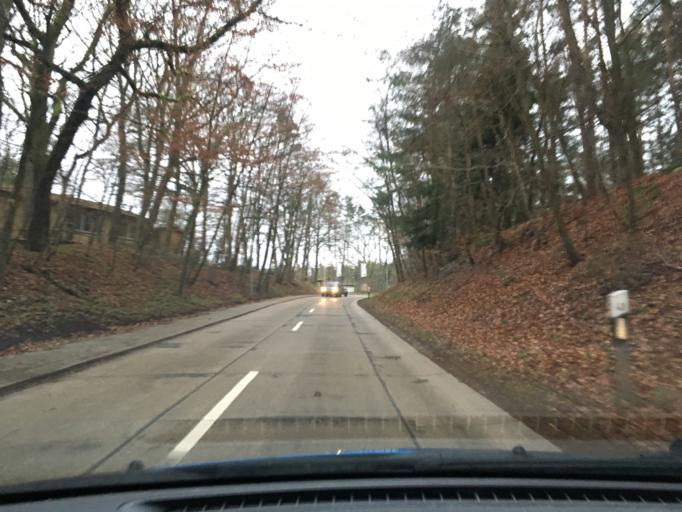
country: DE
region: Lower Saxony
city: Tosterglope
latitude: 53.2604
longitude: 10.8050
